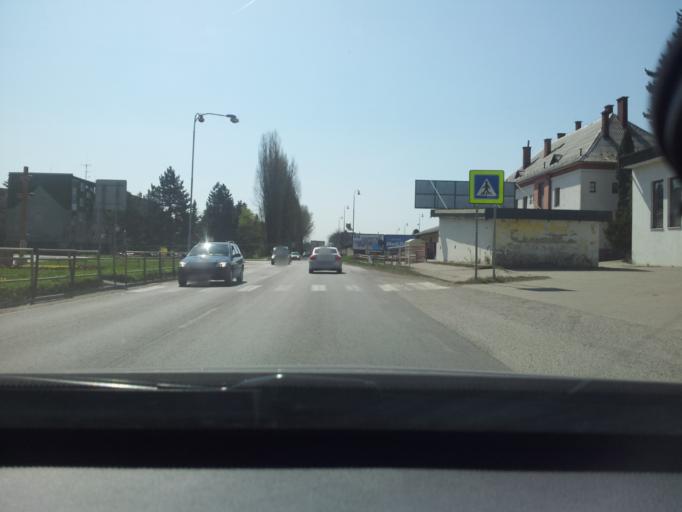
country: SK
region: Nitriansky
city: Banovce nad Bebravou
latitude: 48.7209
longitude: 18.2517
